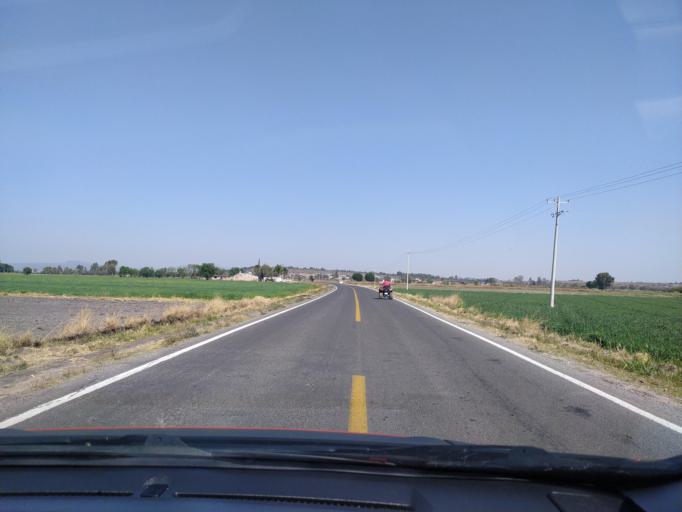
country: MX
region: Guanajuato
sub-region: San Francisco del Rincon
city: San Ignacio de Hidalgo
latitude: 20.8442
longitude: -101.8482
